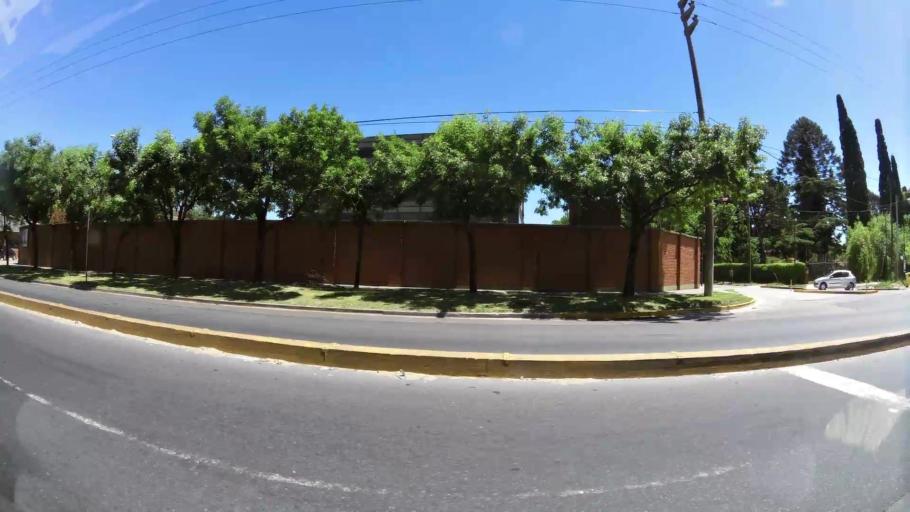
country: AR
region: Buenos Aires
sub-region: Partido de San Isidro
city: San Isidro
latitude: -34.5028
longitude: -58.5610
